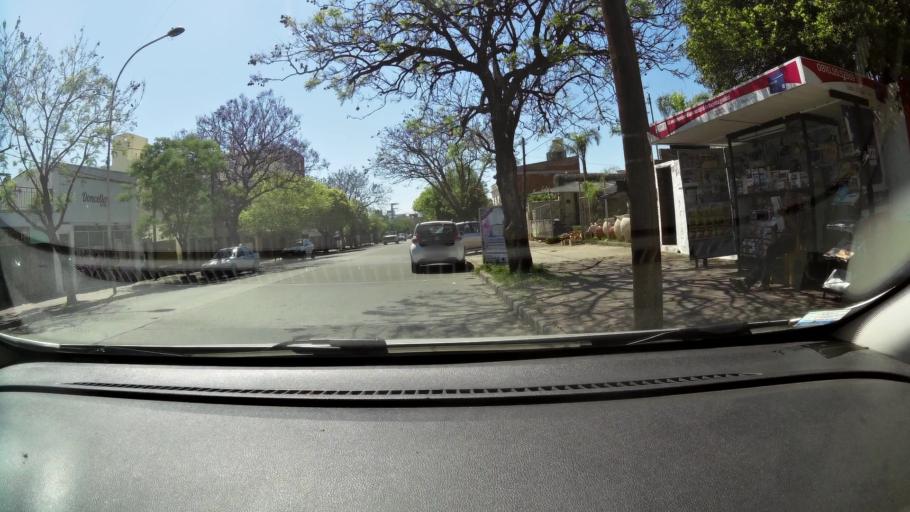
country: AR
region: Cordoba
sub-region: Departamento de Capital
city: Cordoba
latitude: -31.4207
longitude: -64.2113
